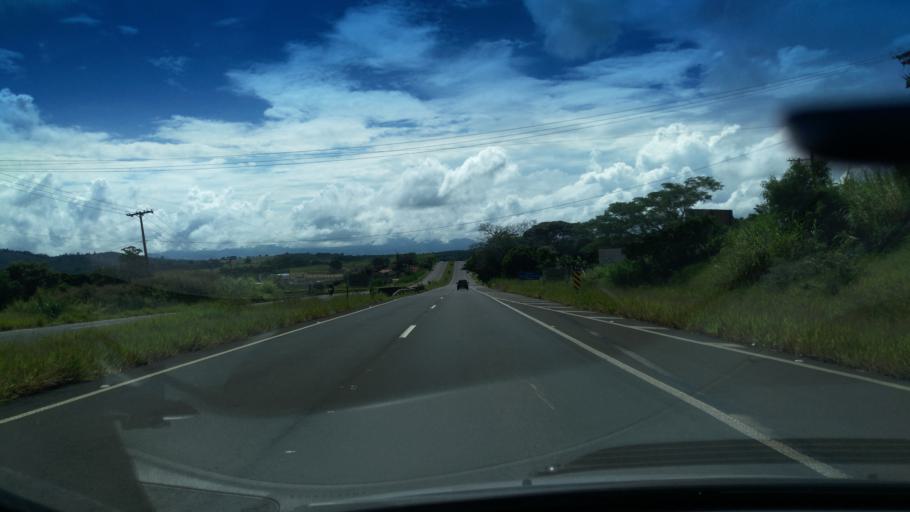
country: BR
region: Sao Paulo
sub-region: Santo Antonio Do Jardim
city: Espirito Santo do Pinhal
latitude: -22.1749
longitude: -46.7478
